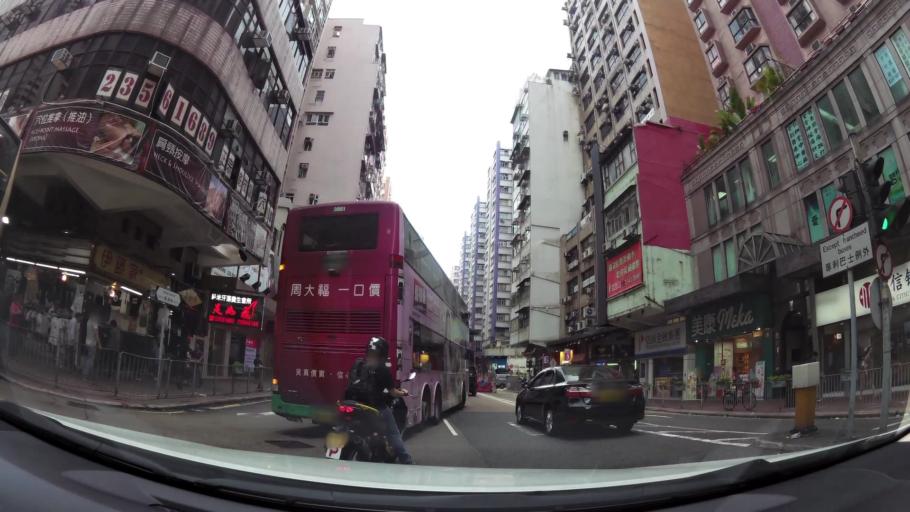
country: HK
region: Kowloon City
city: Kowloon
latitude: 22.3068
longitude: 114.1867
